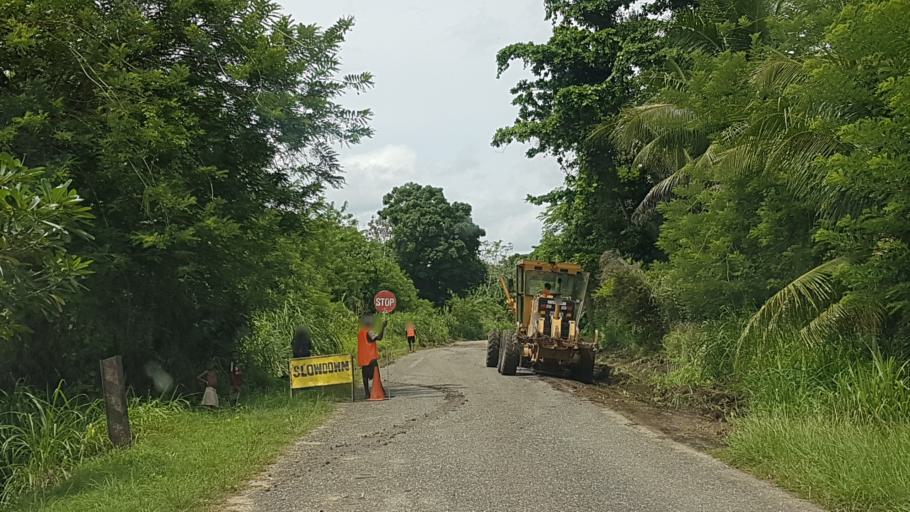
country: PG
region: Madang
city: Madang
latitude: -4.5906
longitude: 145.5319
